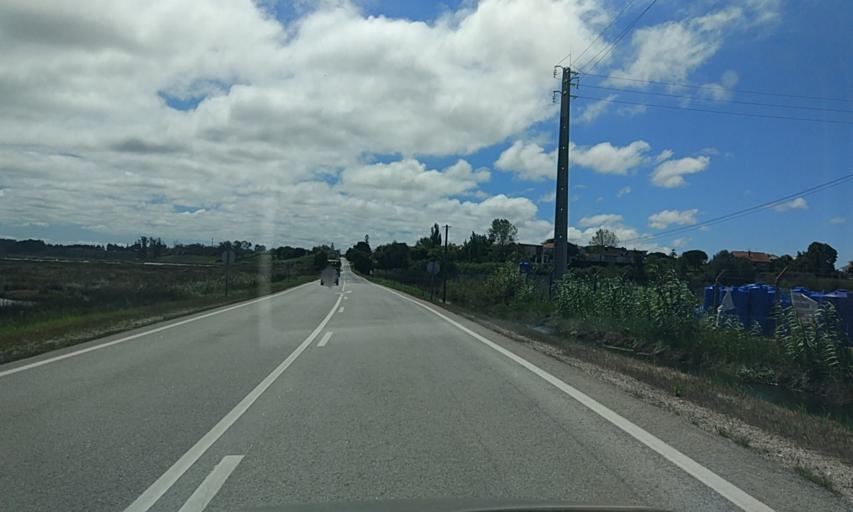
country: PT
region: Aveiro
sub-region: Vagos
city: Vagos
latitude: 40.5712
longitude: -8.6816
